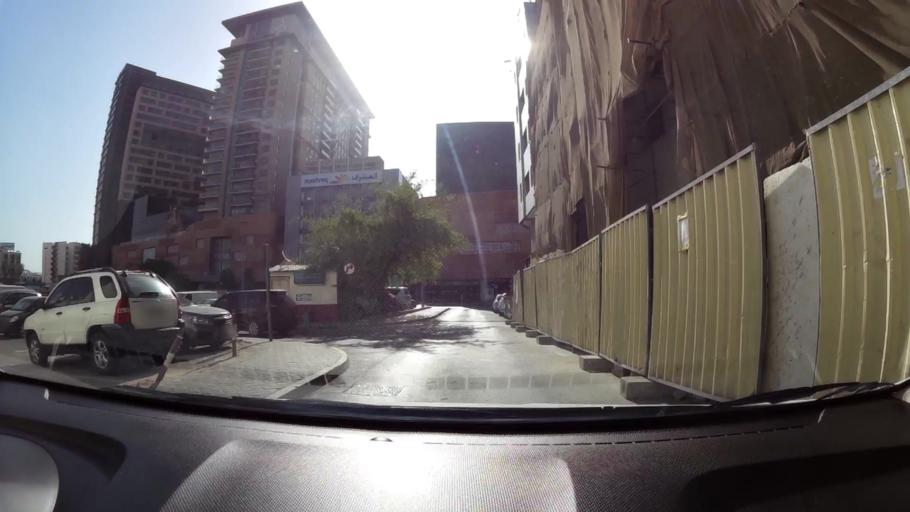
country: AE
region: Ash Shariqah
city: Sharjah
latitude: 25.2679
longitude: 55.3154
